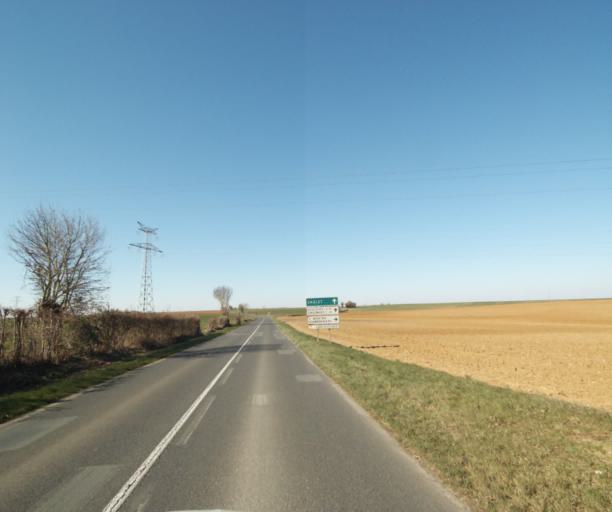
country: FR
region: Poitou-Charentes
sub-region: Departement des Deux-Sevres
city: Saint-Maxire
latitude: 46.3609
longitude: -0.4862
